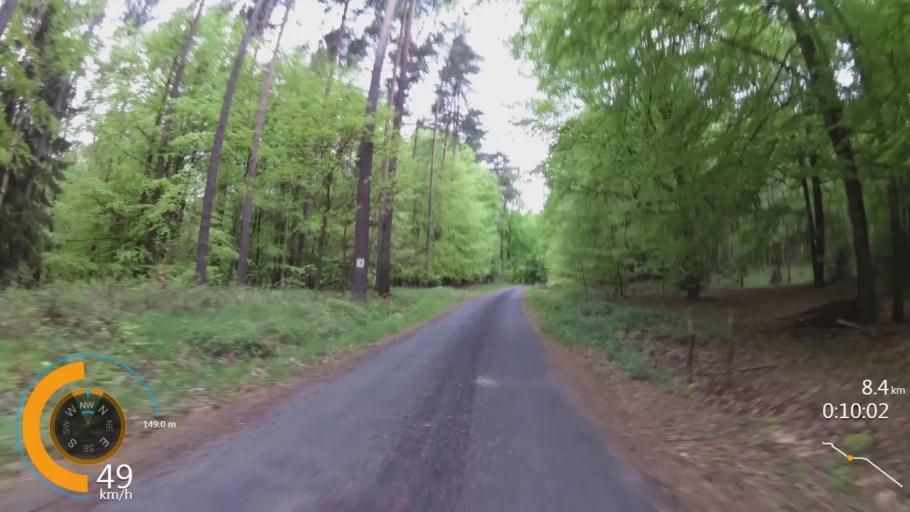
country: PL
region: West Pomeranian Voivodeship
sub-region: Powiat drawski
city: Wierzchowo
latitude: 53.5042
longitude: 16.1277
